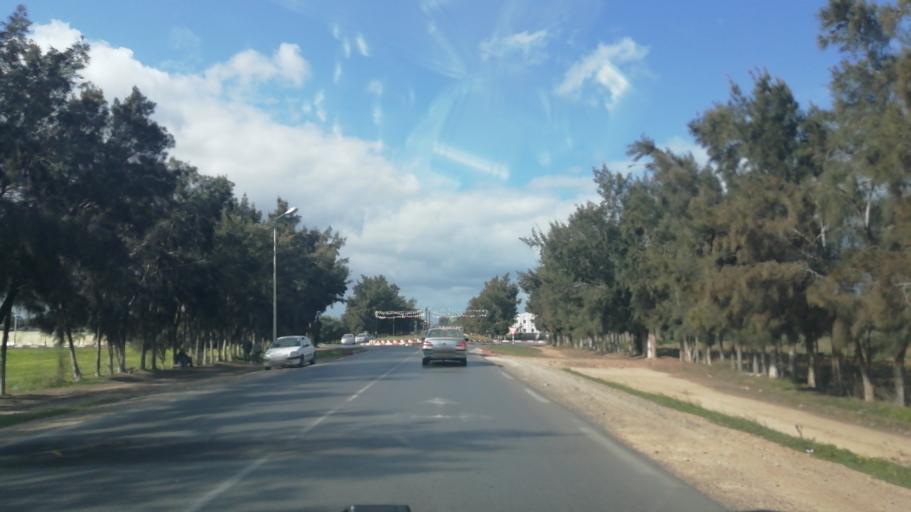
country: DZ
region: Relizane
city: Mazouna
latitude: 36.2558
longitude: 0.5837
